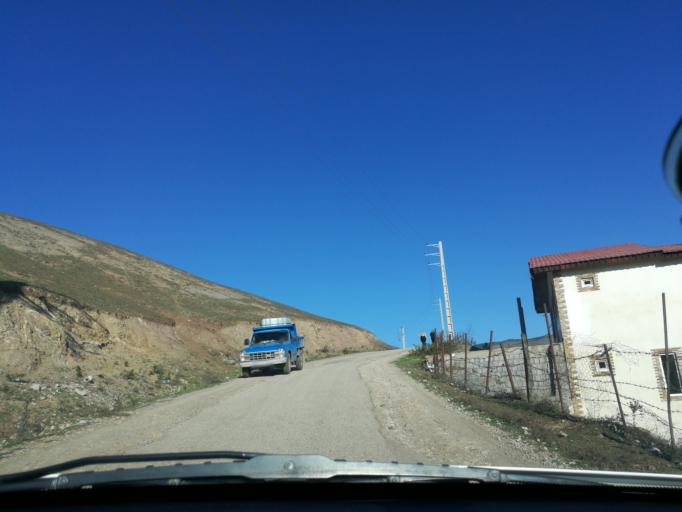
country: IR
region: Mazandaran
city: `Abbasabad
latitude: 36.5589
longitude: 51.1917
